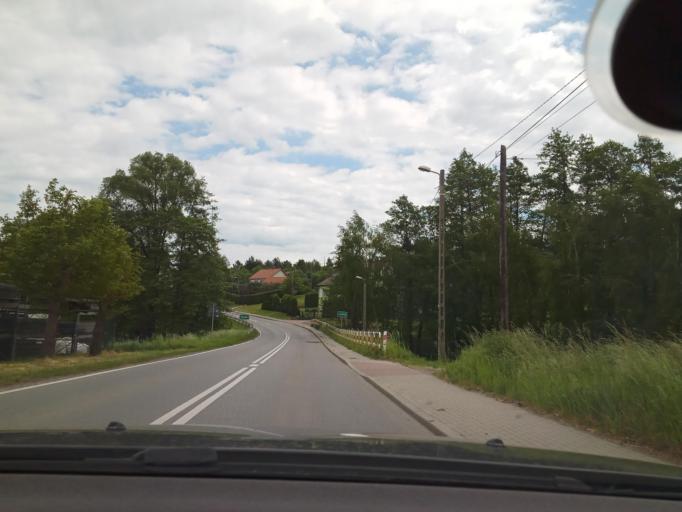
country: PL
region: Lesser Poland Voivodeship
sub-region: Powiat wielicki
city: Trabki
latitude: 49.9549
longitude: 20.1531
